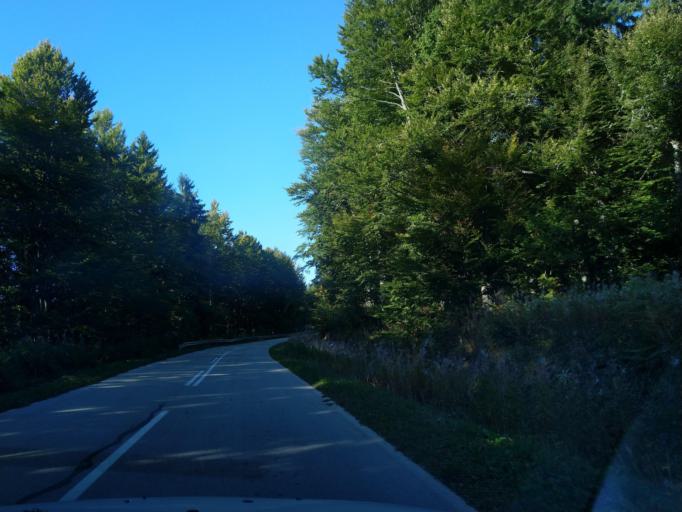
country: RS
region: Central Serbia
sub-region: Moravicki Okrug
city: Ivanjica
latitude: 43.4137
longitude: 20.2657
